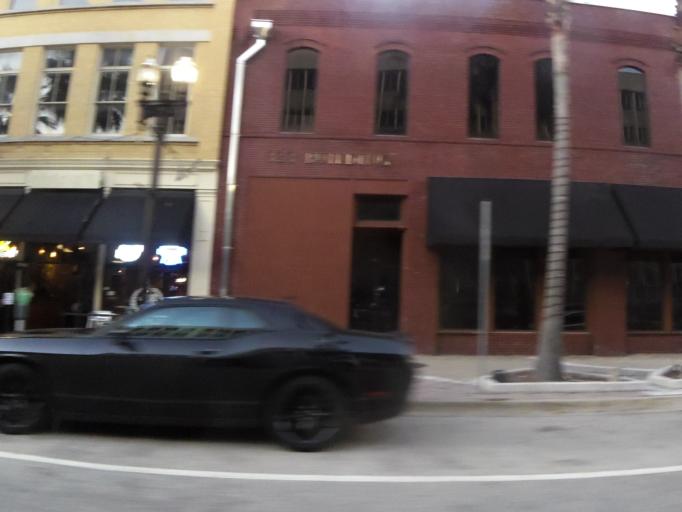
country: US
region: Florida
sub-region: Duval County
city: Jacksonville
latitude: 30.3254
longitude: -81.6536
